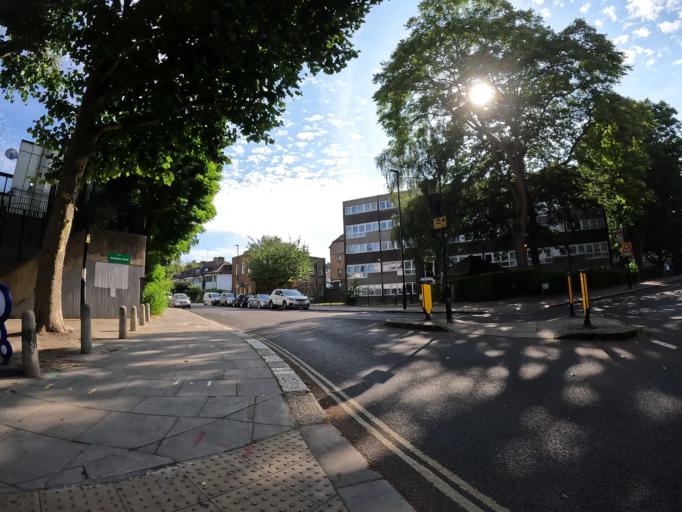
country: GB
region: England
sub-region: Greater London
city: Belsize Park
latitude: 51.5643
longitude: -0.1738
